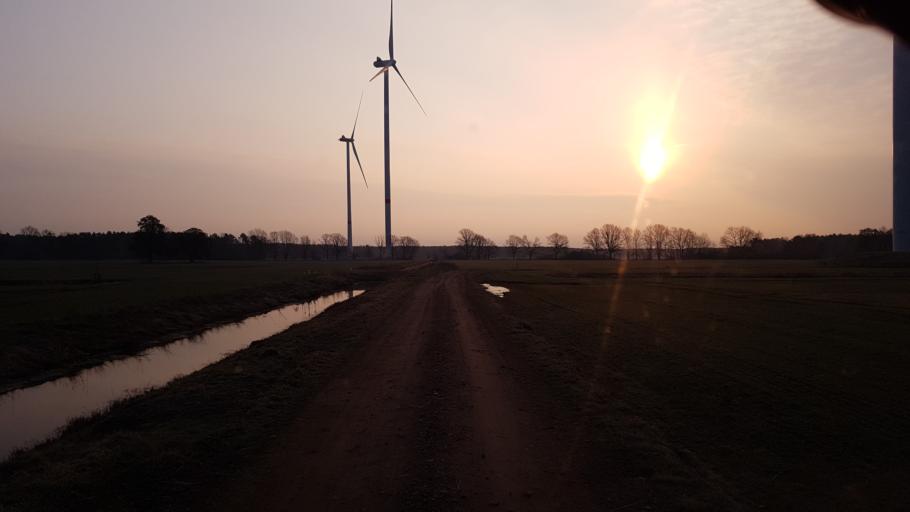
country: DE
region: Brandenburg
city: Falkenberg
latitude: 51.5720
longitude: 13.3007
